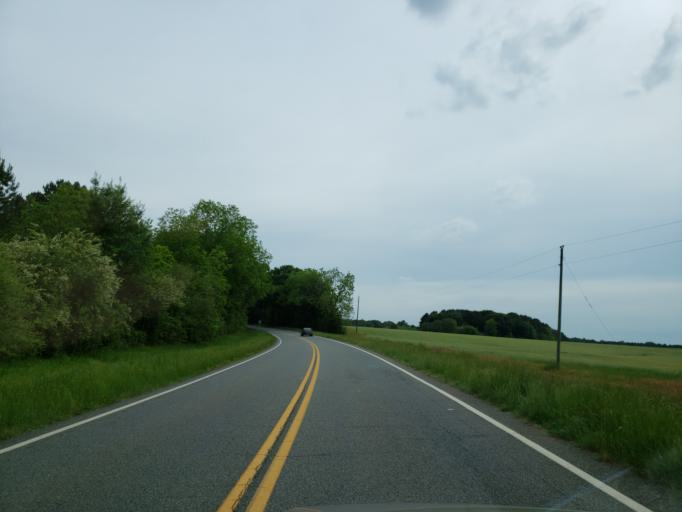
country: US
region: Georgia
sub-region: Macon County
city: Marshallville
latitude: 32.4114
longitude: -83.8655
